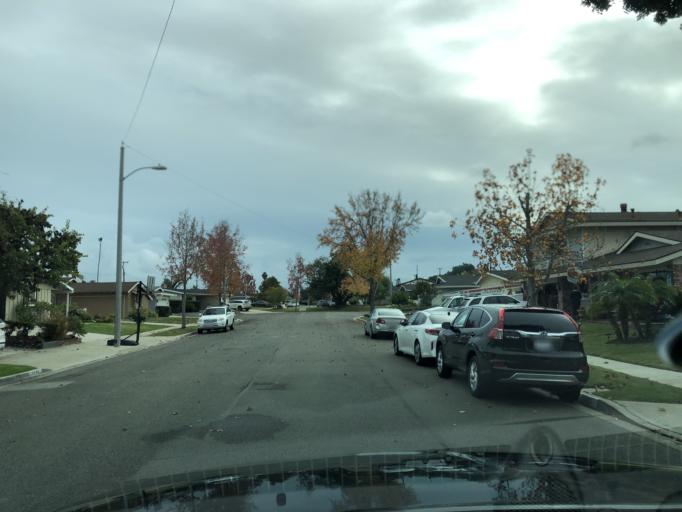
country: US
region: California
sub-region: Orange County
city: Fountain Valley
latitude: 33.6900
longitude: -117.9296
